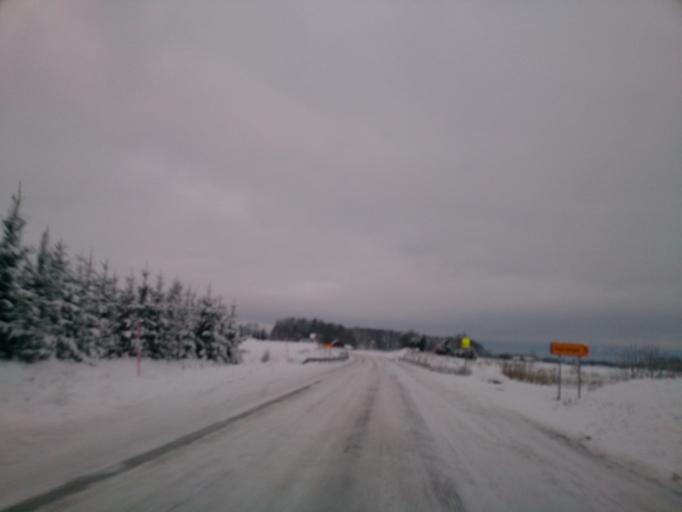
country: SE
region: OEstergoetland
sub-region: Linkopings Kommun
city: Linghem
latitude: 58.4496
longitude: 15.8886
